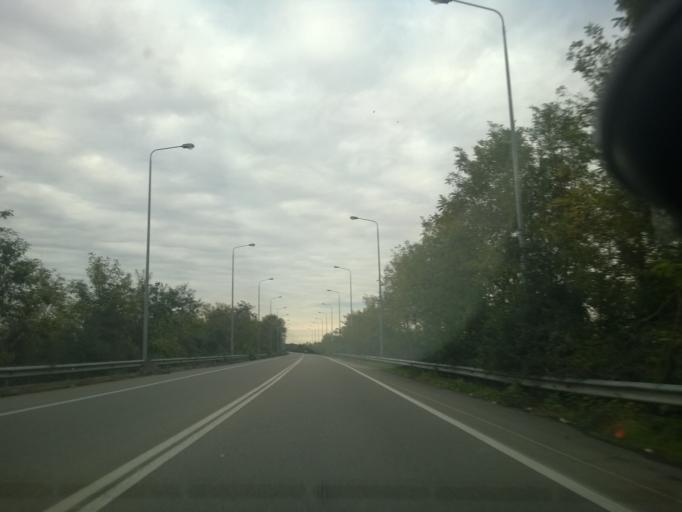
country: GR
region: Central Macedonia
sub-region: Nomos Pellis
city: Karyotissa
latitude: 40.7782
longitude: 22.3196
